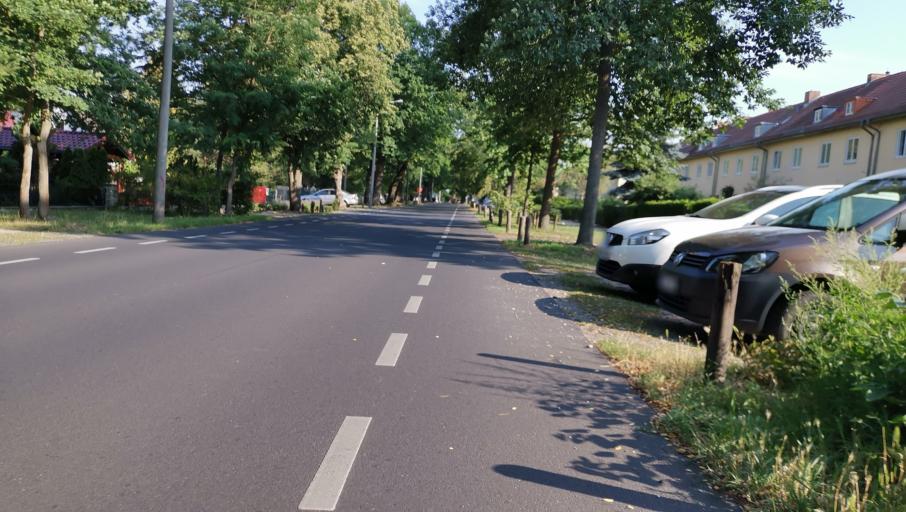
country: DE
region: Brandenburg
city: Potsdam
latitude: 52.3860
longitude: 13.0134
